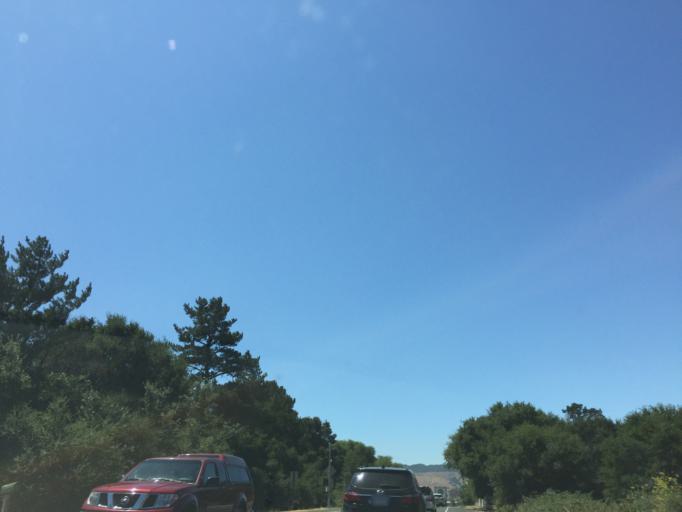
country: US
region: California
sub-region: Sonoma County
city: Temelec
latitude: 38.2416
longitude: -122.4500
